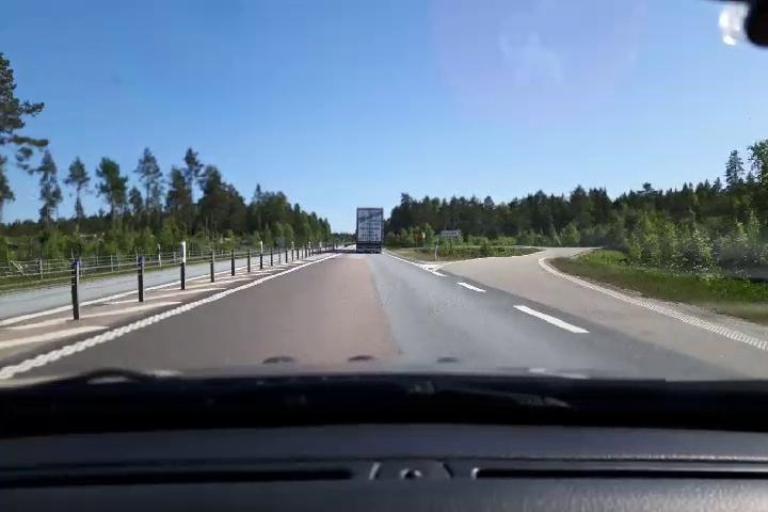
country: SE
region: Gaevleborg
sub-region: Soderhamns Kommun
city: Soderhamn
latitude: 61.2648
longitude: 17.0306
